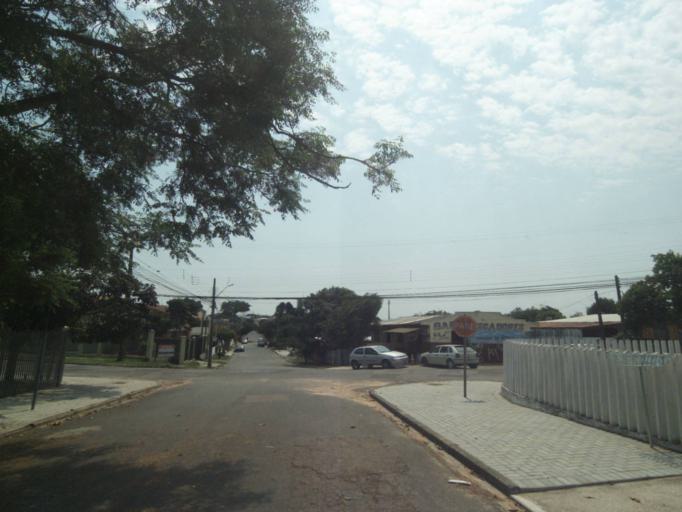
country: BR
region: Parana
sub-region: Sao Jose Dos Pinhais
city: Sao Jose dos Pinhais
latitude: -25.5398
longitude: -49.2424
